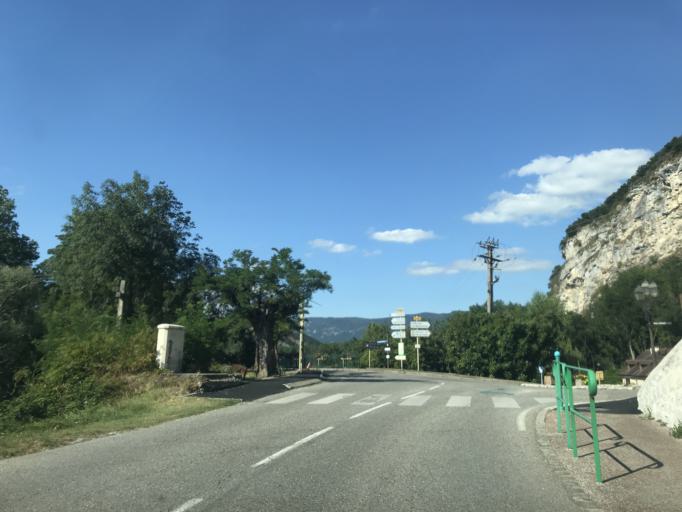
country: FR
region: Rhone-Alpes
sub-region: Departement de l'Ain
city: Culoz
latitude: 45.8101
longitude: 5.7948
